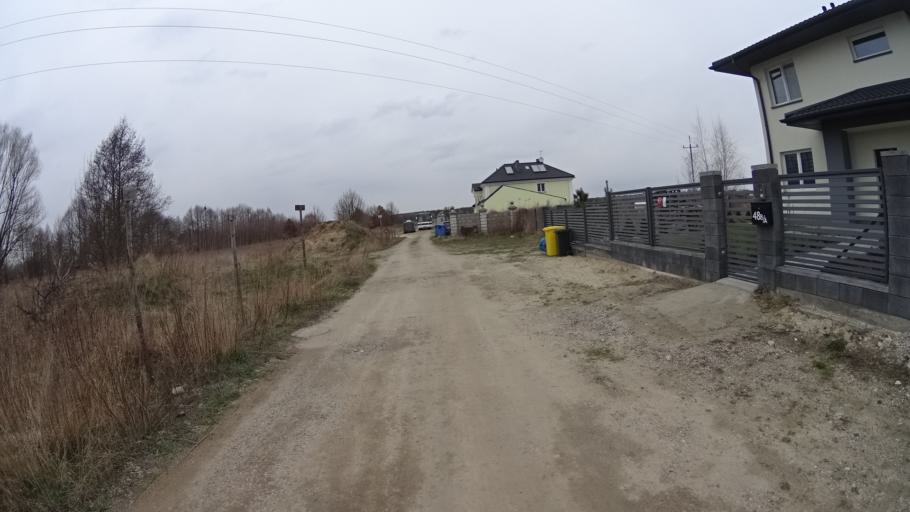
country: PL
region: Masovian Voivodeship
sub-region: Powiat warszawski zachodni
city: Hornowek
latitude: 52.2651
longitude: 20.7855
